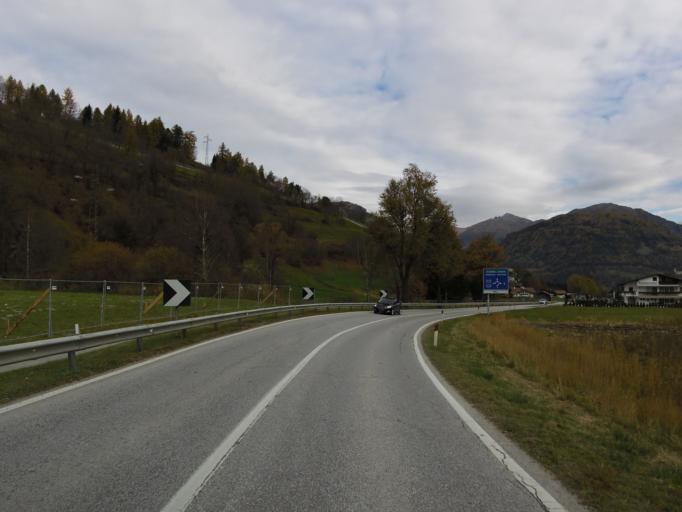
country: IT
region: Trentino-Alto Adige
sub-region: Bolzano
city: Vipiteno
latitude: 46.8868
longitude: 11.4148
